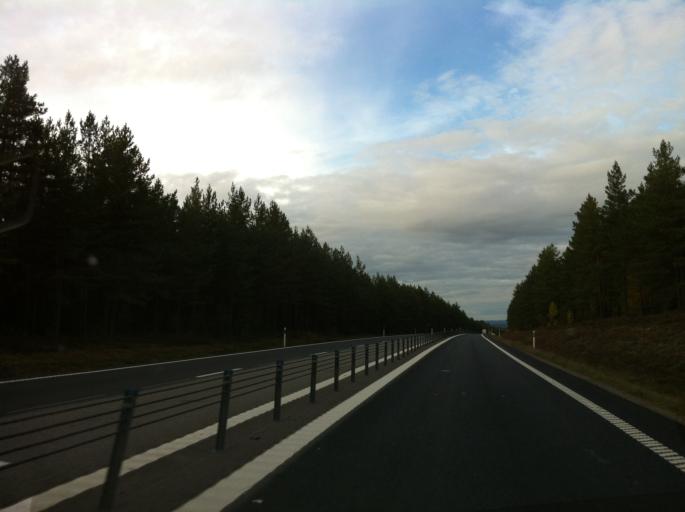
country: SE
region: OErebro
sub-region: Askersunds Kommun
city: Asbro
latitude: 58.9994
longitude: 15.0425
